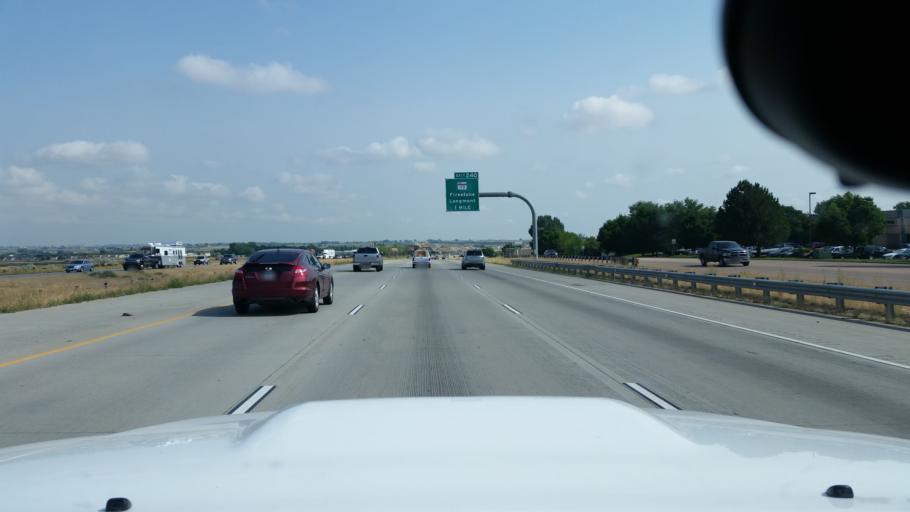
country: US
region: Colorado
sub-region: Weld County
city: Firestone
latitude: 40.1420
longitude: -104.9801
